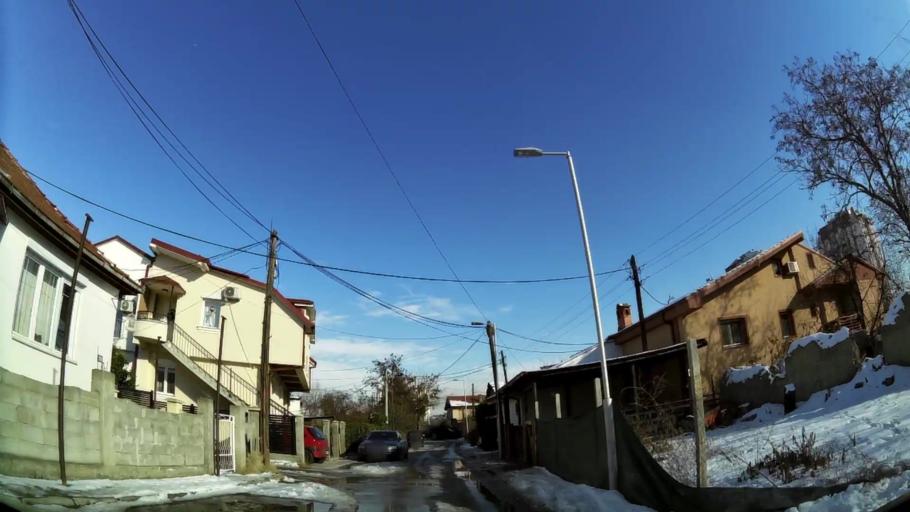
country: MK
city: Krushopek
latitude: 42.0071
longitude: 21.3791
